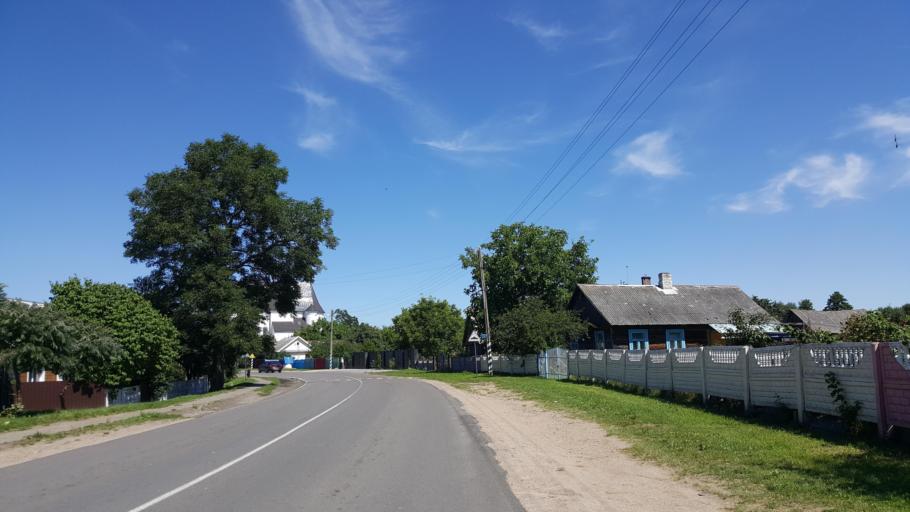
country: BY
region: Brest
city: Charnawchytsy
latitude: 52.2161
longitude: 23.7407
